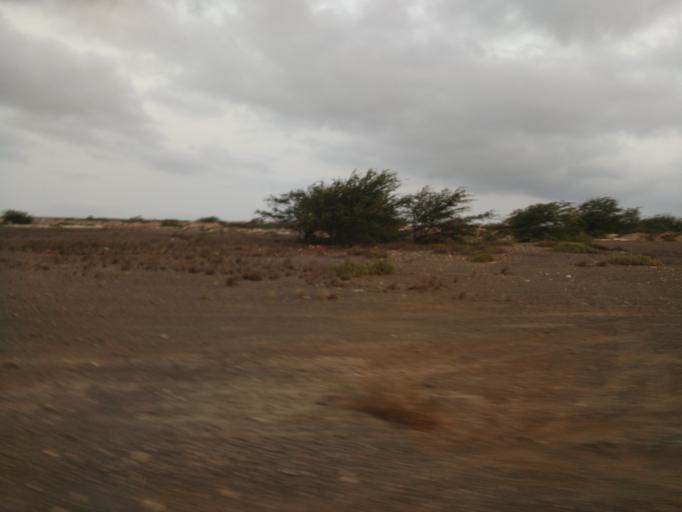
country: CV
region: Sal
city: Santa Maria
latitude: 16.6637
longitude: -22.9337
